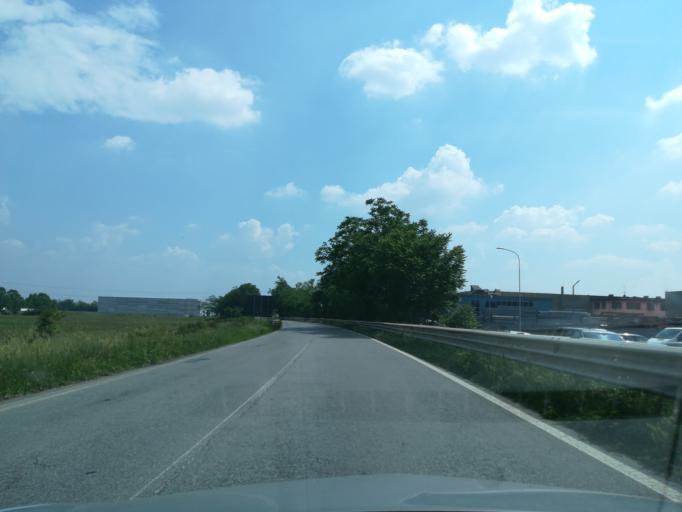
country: IT
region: Lombardy
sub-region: Provincia di Bergamo
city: Costa di Mezzate
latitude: 45.6537
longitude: 9.8077
